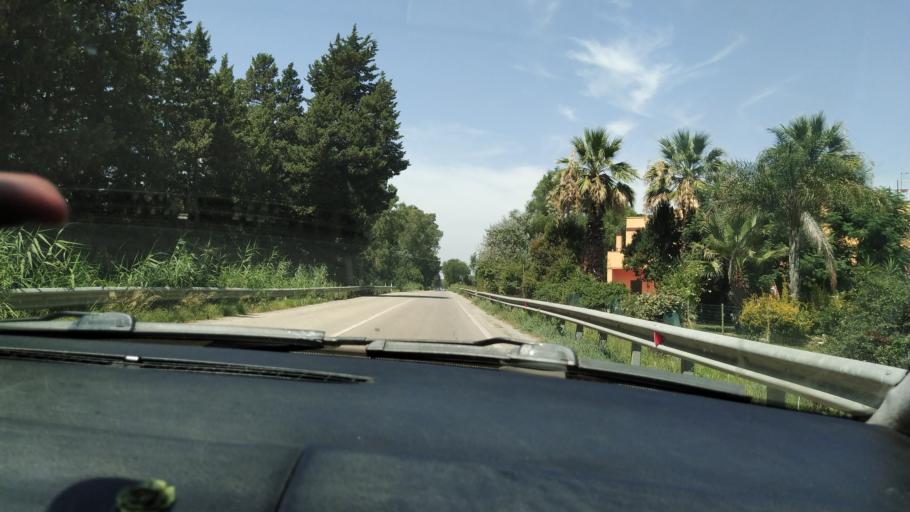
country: IT
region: Apulia
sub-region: Provincia di Taranto
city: Marina di Ginosa
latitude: 40.3725
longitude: 16.8053
